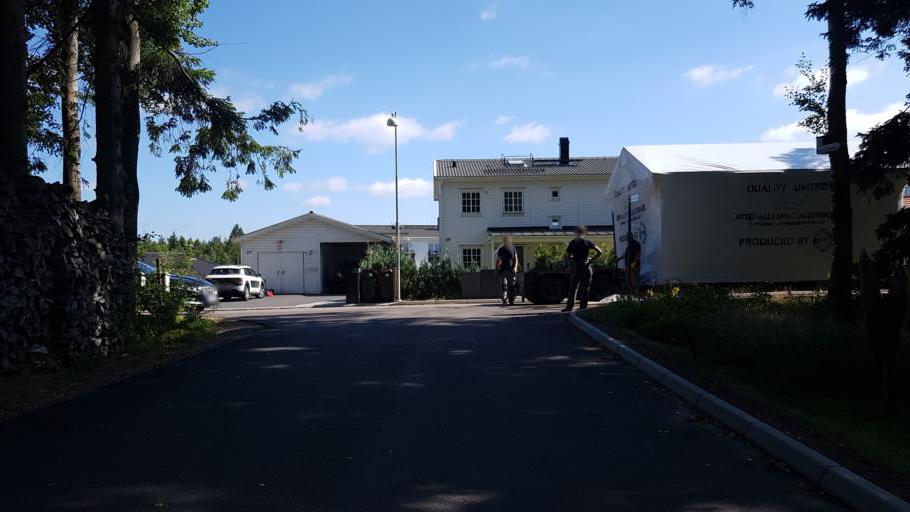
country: SE
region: Vaestra Goetaland
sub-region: Partille Kommun
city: Ojersjo
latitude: 57.6841
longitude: 12.0956
